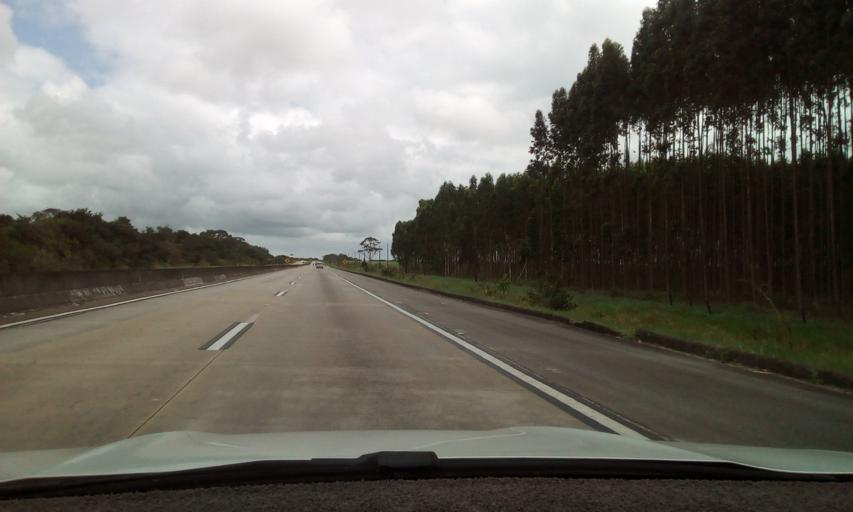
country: BR
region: Paraiba
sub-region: Santa Rita
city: Santa Rita
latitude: -7.0496
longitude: -35.0409
